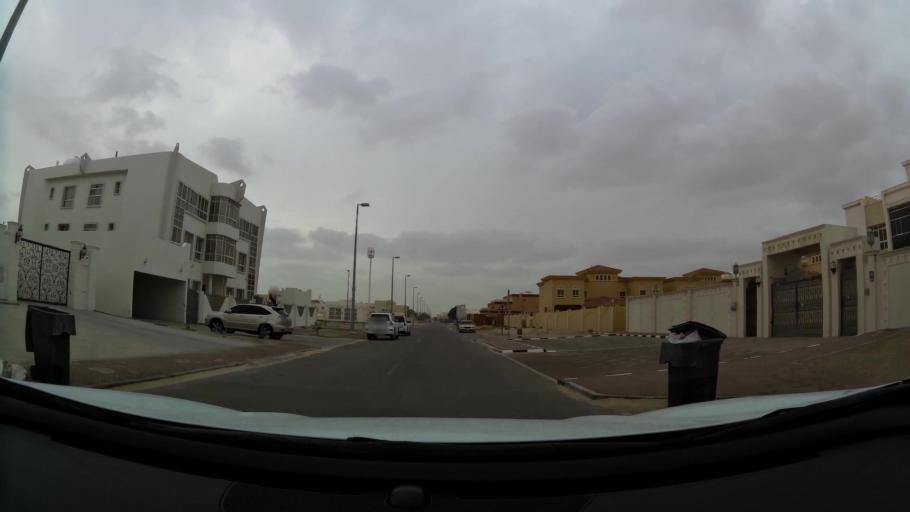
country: AE
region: Abu Dhabi
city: Abu Dhabi
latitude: 24.3791
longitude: 54.6491
